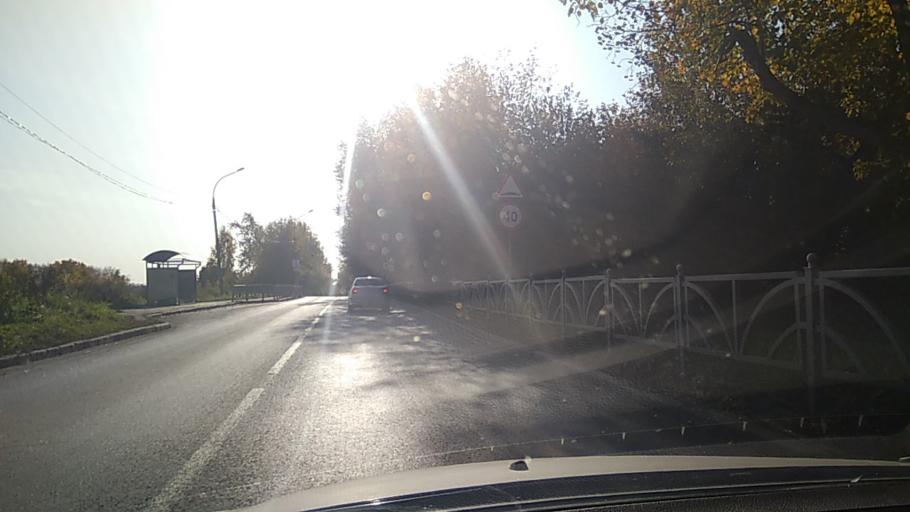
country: RU
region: Sverdlovsk
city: Yekaterinburg
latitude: 56.7772
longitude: 60.6405
